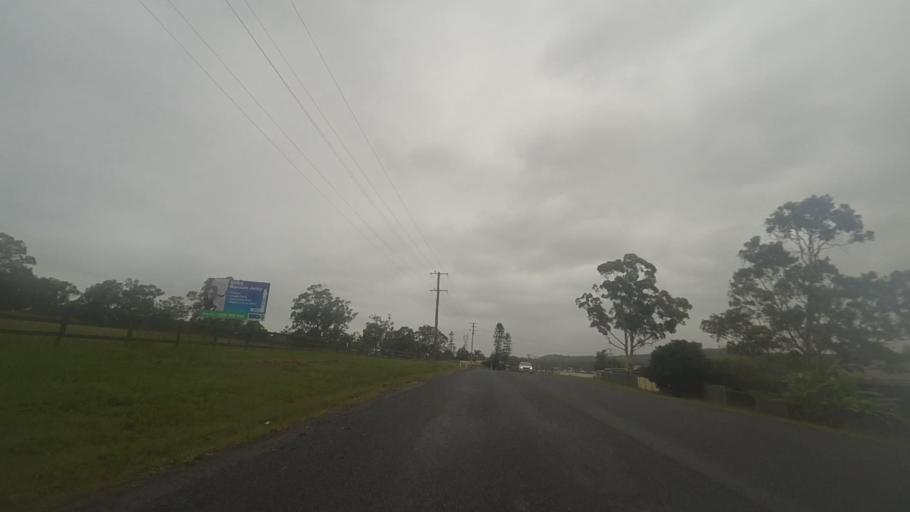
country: AU
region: New South Wales
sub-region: Port Stephens Shire
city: Port Stephens
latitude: -32.6520
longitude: 151.9719
